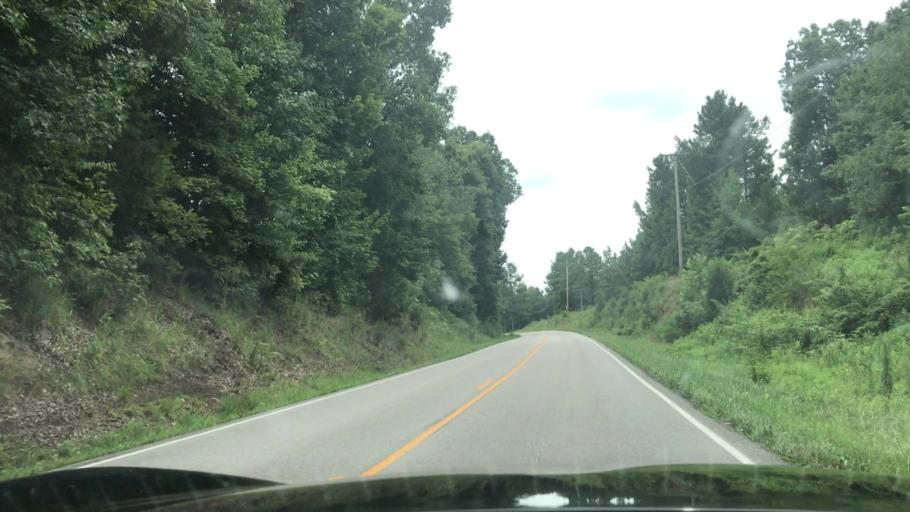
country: US
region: Kentucky
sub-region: Ohio County
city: Oak Grove
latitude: 37.1931
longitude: -86.8834
